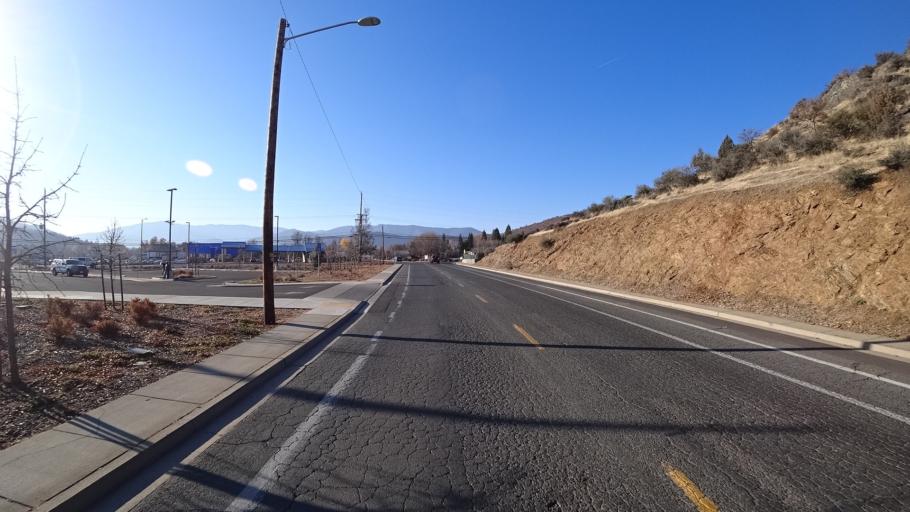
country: US
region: California
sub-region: Siskiyou County
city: Yreka
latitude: 41.7128
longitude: -122.6436
